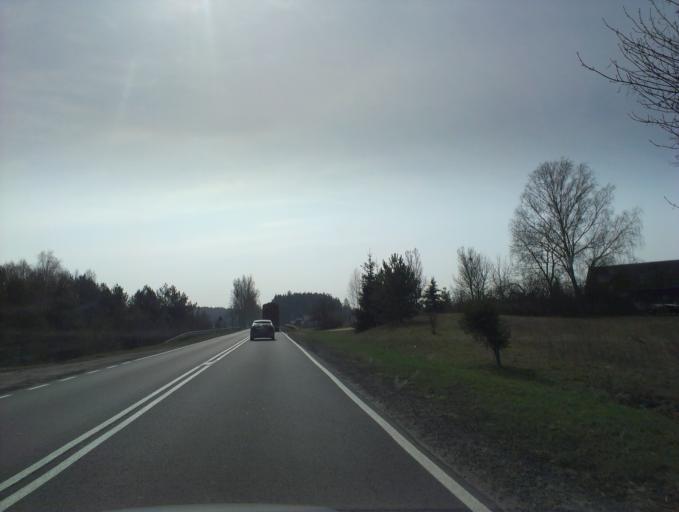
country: PL
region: Greater Poland Voivodeship
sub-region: Powiat zlotowski
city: Tarnowka
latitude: 53.2638
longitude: 16.7816
